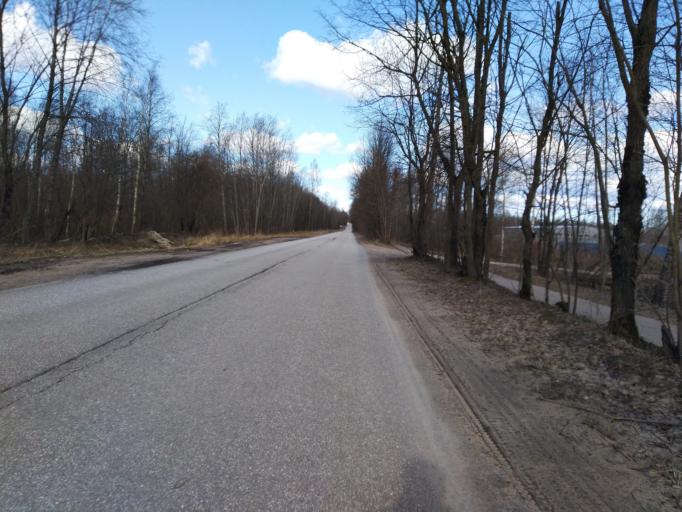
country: RU
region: Leningrad
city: Novoye Devyatkino
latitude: 60.0979
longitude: 30.4764
